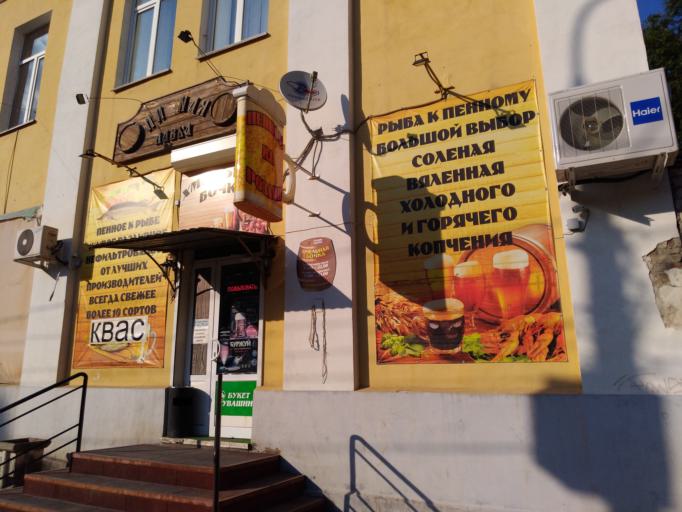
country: RU
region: Volgograd
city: Volgograd
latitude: 48.7184
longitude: 44.5164
